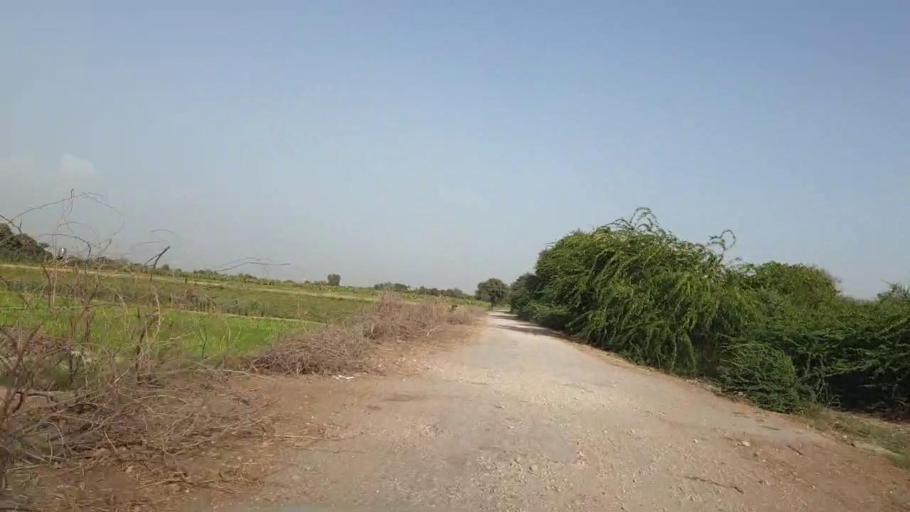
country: PK
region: Sindh
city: Tando Ghulam Ali
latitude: 25.0834
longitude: 68.8827
